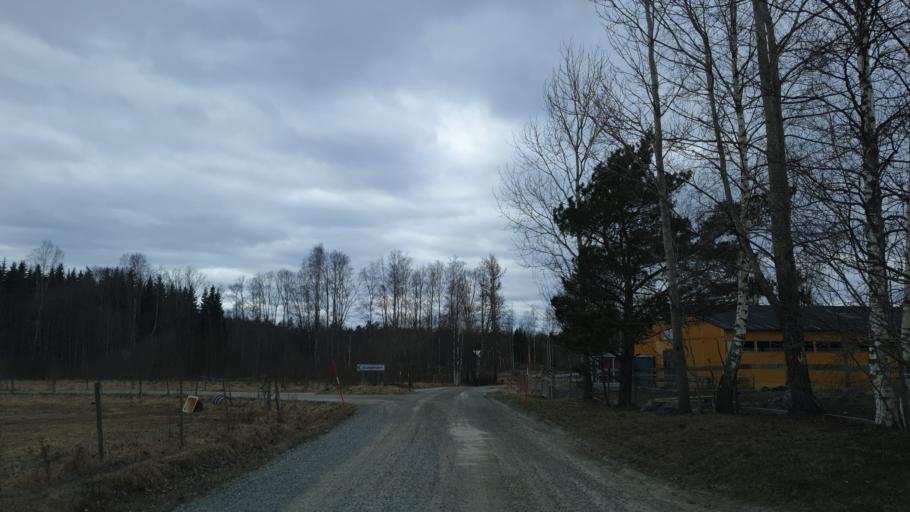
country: SE
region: OErebro
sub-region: Nora Kommun
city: As
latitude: 59.6011
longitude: 14.9078
